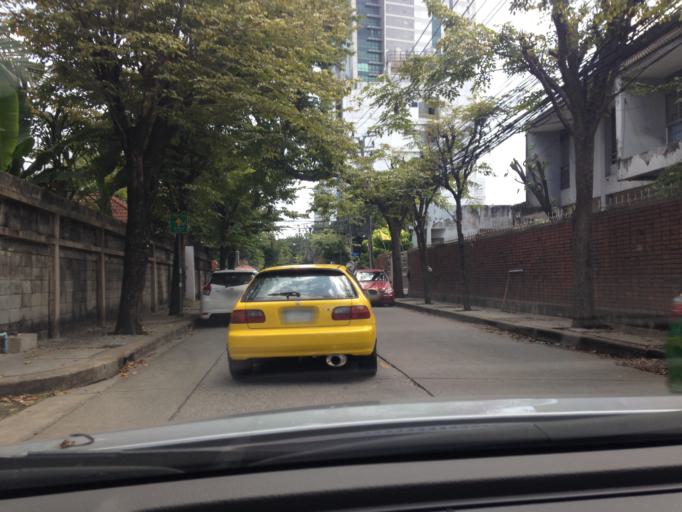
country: TH
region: Bangkok
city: Bang Sue
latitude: 13.8001
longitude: 100.5584
